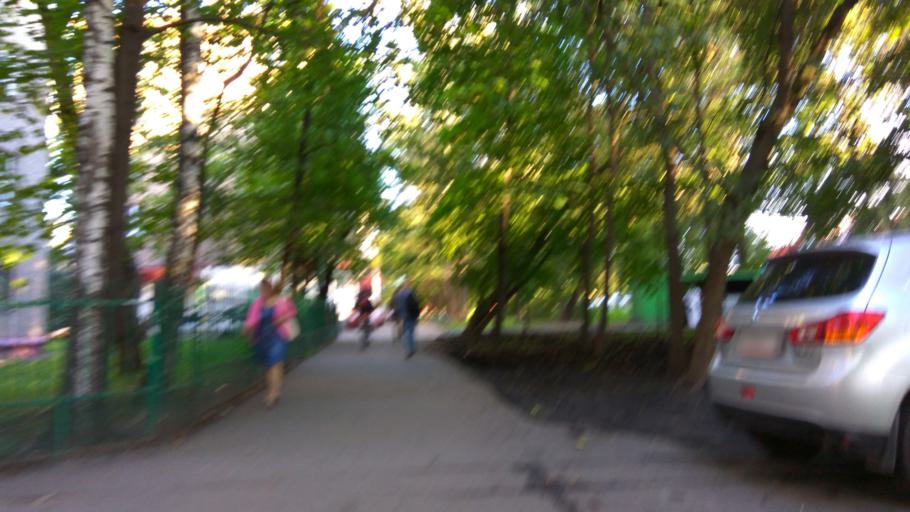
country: RU
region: Moscow
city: Likhobory
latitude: 55.8390
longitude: 37.5730
